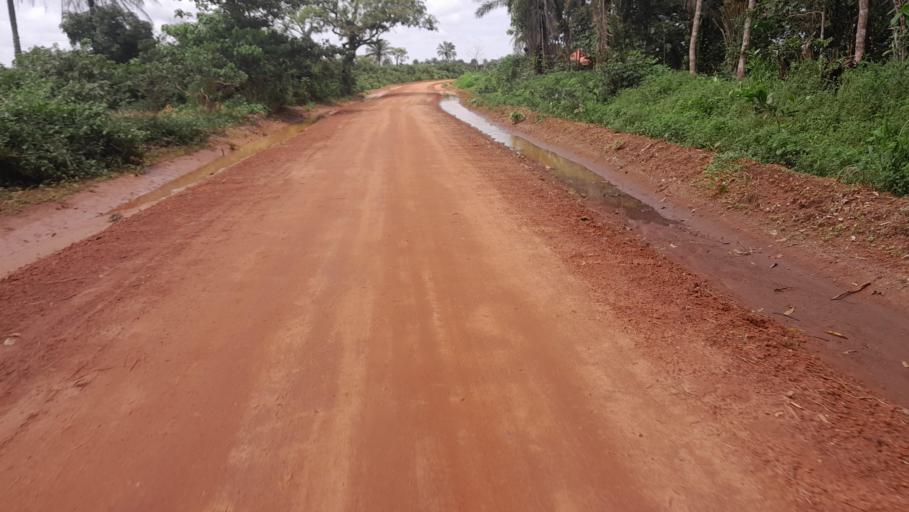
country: GN
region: Boke
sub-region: Boffa
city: Boffa
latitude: 10.0422
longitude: -13.8736
